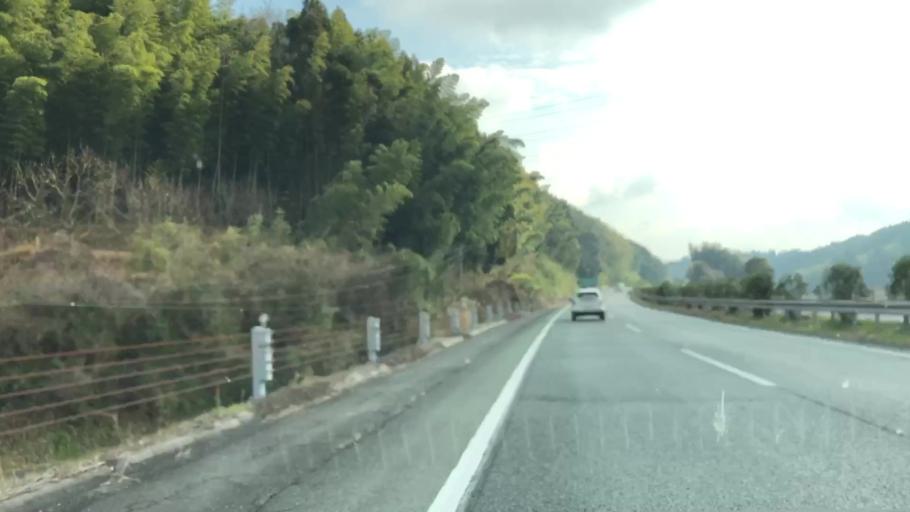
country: JP
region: Kumamoto
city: Yamaga
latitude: 33.0394
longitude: 130.5700
